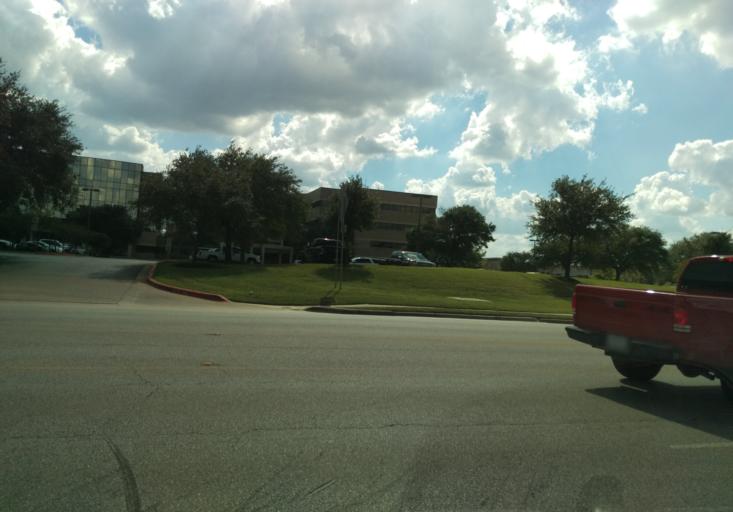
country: US
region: Texas
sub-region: Brazos County
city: College Station
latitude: 30.5827
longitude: -96.2911
